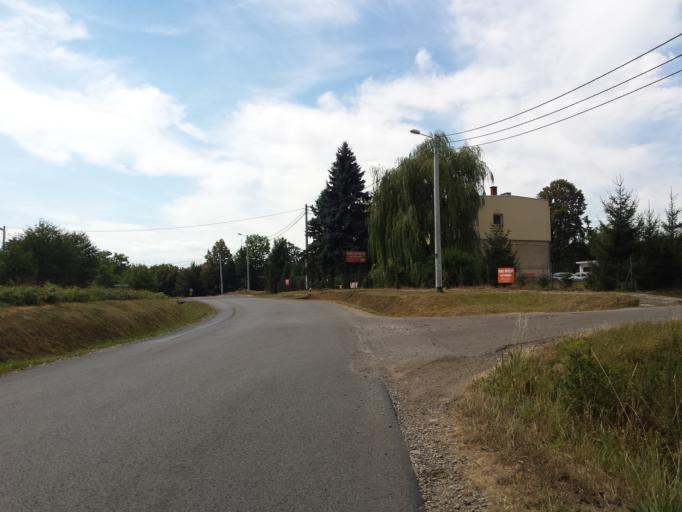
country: PL
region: Subcarpathian Voivodeship
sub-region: Powiat przemyski
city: Fredropol
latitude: 49.6984
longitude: 22.7474
